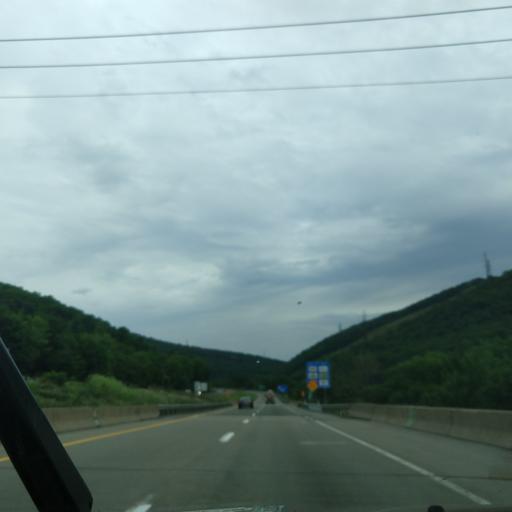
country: US
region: Pennsylvania
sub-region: Lackawanna County
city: Chinchilla
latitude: 41.4737
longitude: -75.6798
